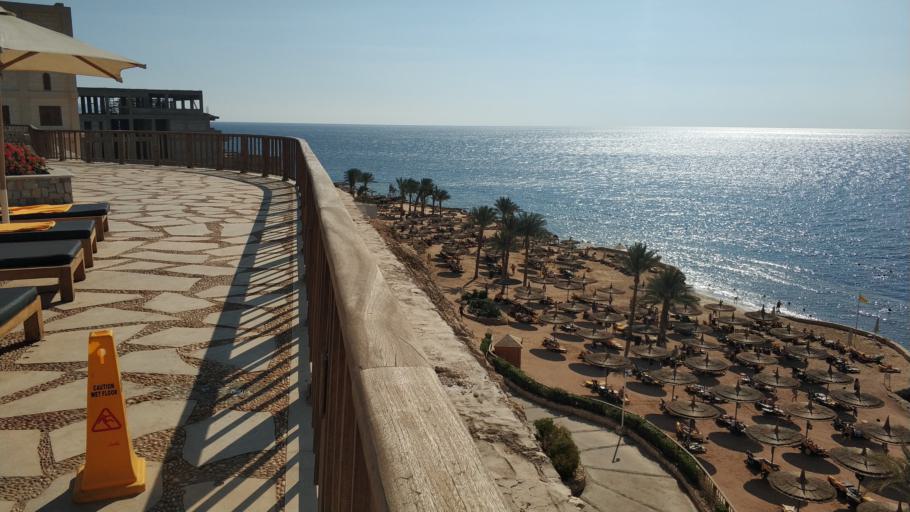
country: EG
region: South Sinai
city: Sharm el-Sheikh
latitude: 27.9154
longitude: 34.3610
